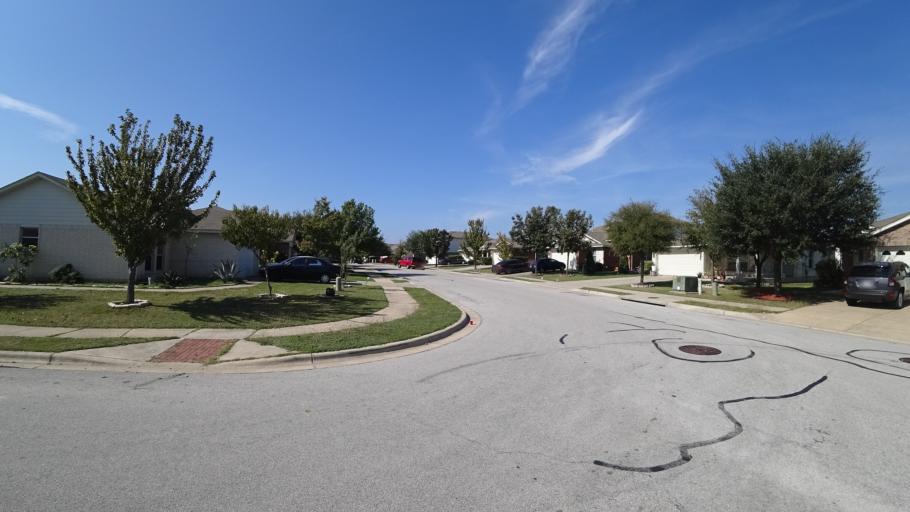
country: US
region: Texas
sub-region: Travis County
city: Pflugerville
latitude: 30.4288
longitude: -97.6385
